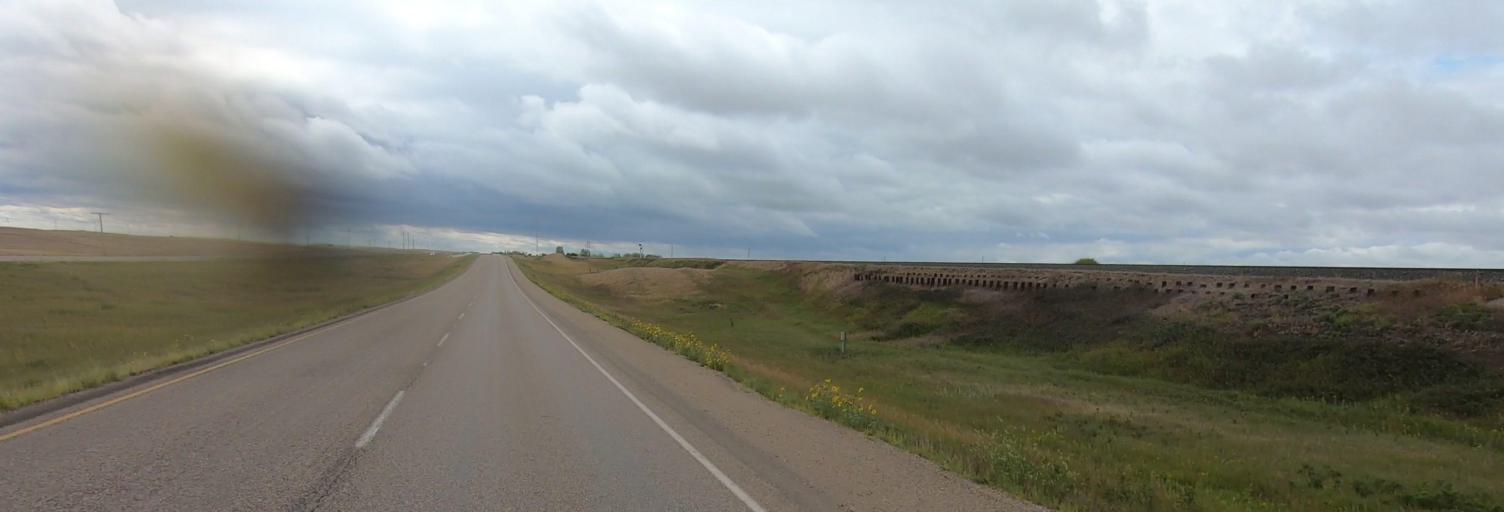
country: CA
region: Saskatchewan
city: Gravelbourg
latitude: 50.4262
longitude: -106.9318
